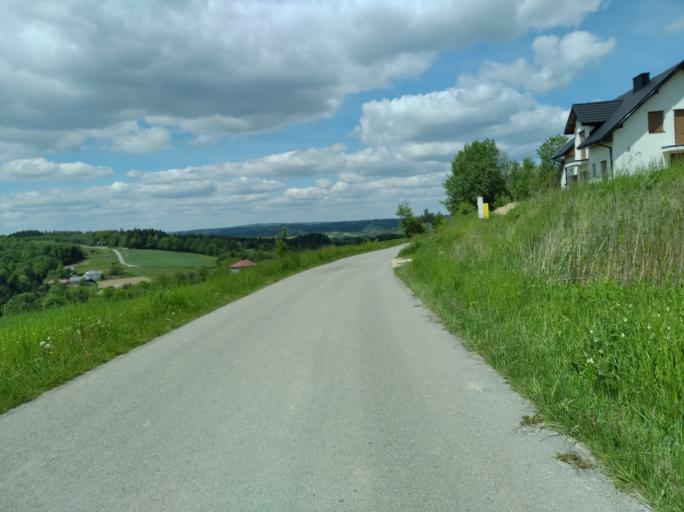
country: PL
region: Subcarpathian Voivodeship
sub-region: Powiat ropczycko-sedziszowski
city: Wielopole Skrzynskie
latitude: 49.9248
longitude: 21.6054
